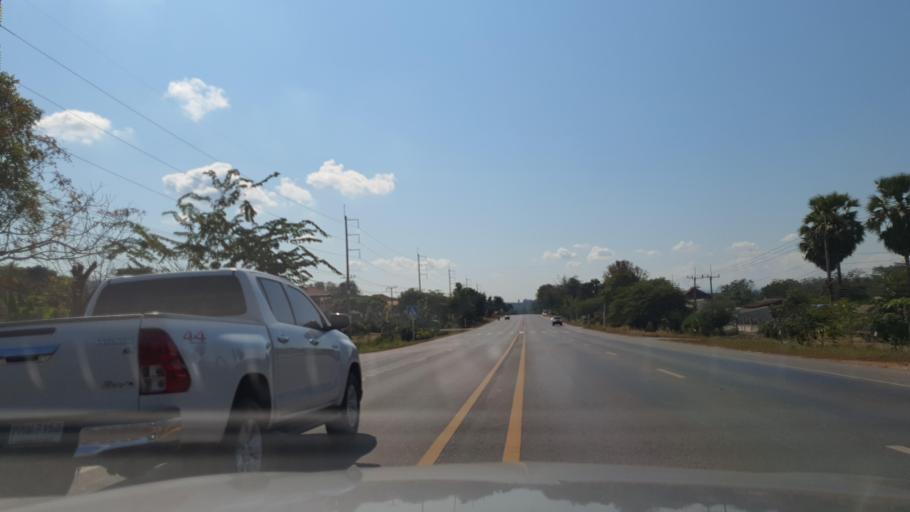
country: TH
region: Nan
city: Tha Wang Pha
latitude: 19.0371
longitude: 100.8026
